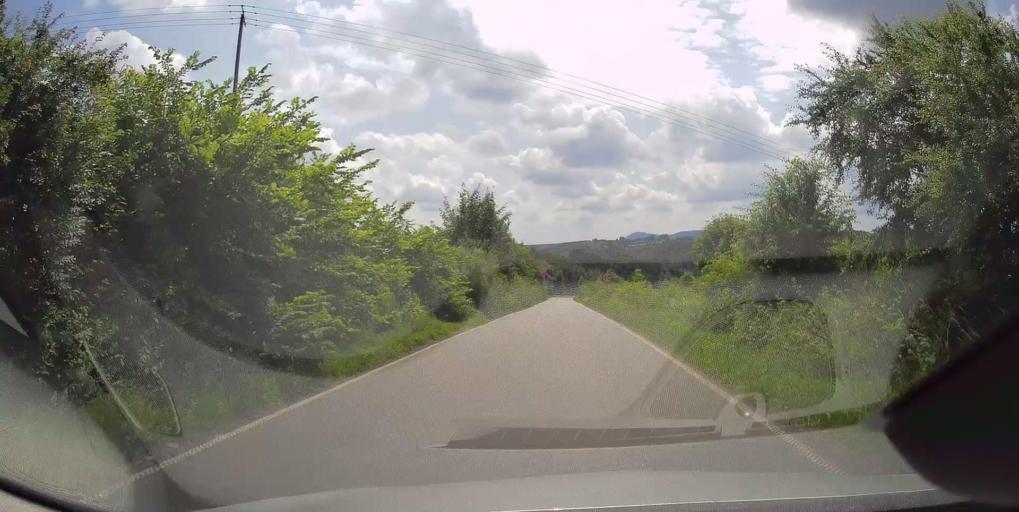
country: PL
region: Lesser Poland Voivodeship
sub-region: Powiat nowosadecki
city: Korzenna
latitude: 49.7061
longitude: 20.7627
